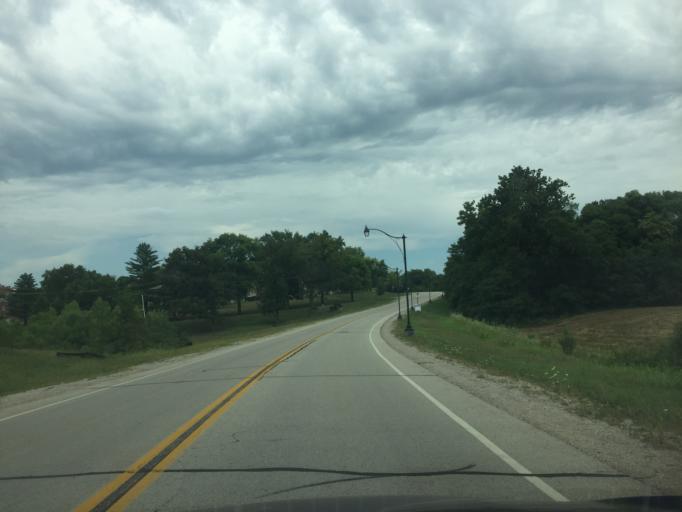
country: US
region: Kansas
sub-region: Leavenworth County
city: Leavenworth
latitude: 39.3431
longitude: -94.9136
